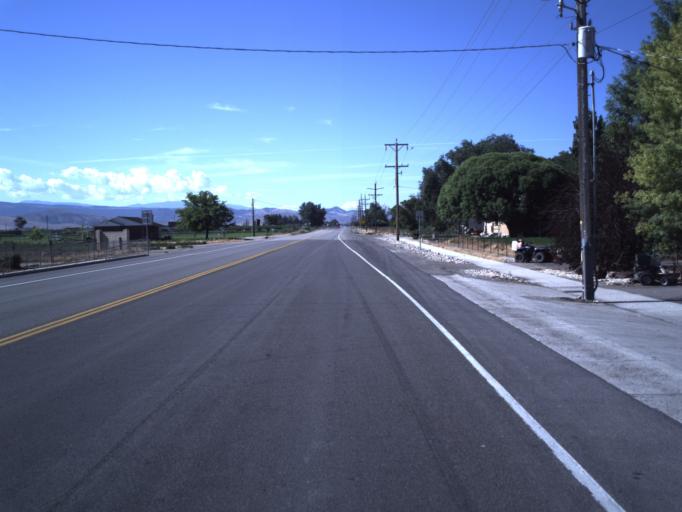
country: US
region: Utah
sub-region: Sanpete County
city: Centerfield
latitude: 39.1185
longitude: -111.8195
